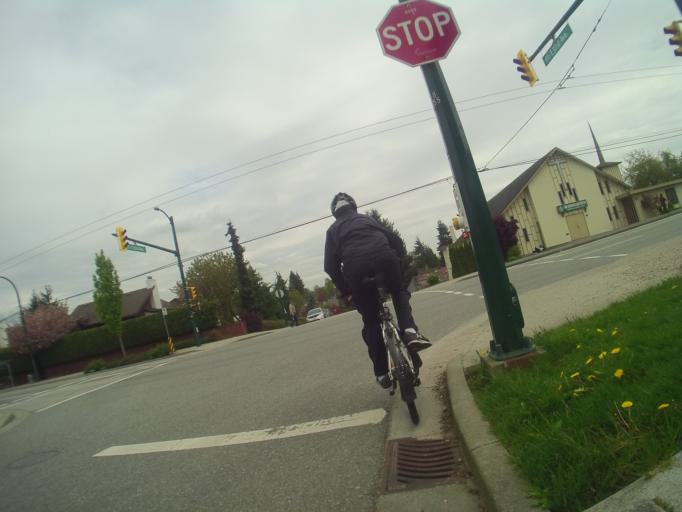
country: CA
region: British Columbia
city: Vancouver
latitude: 49.2425
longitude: -123.0906
